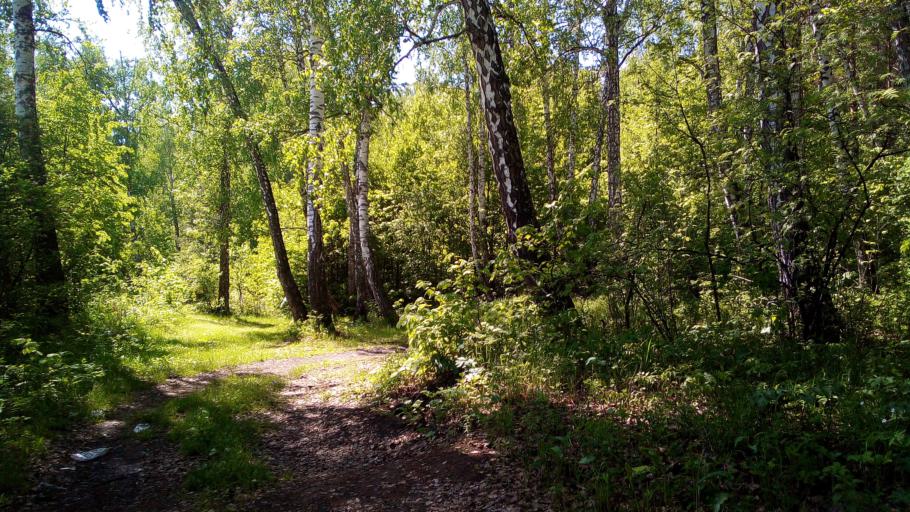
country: RU
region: Chelyabinsk
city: Chebarkul'
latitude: 55.0833
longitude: 60.3820
